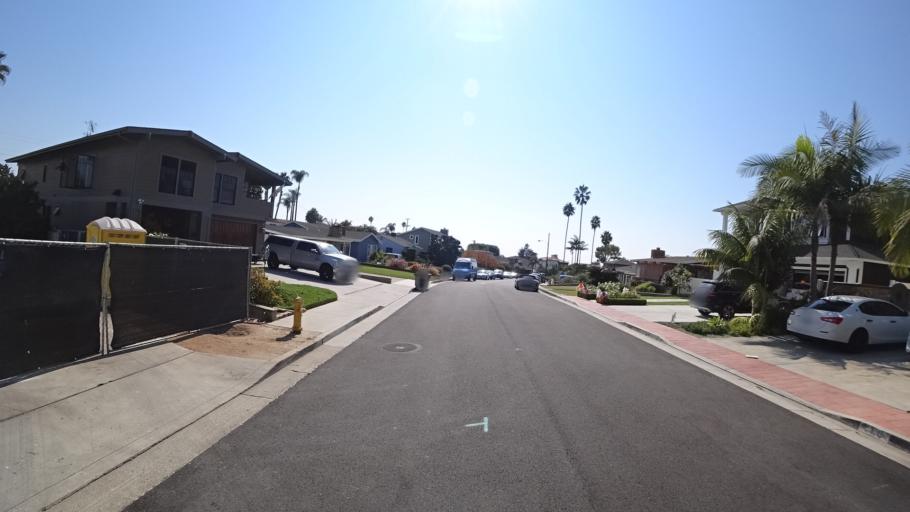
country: US
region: California
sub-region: Orange County
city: San Clemente
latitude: 33.4152
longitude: -117.6093
